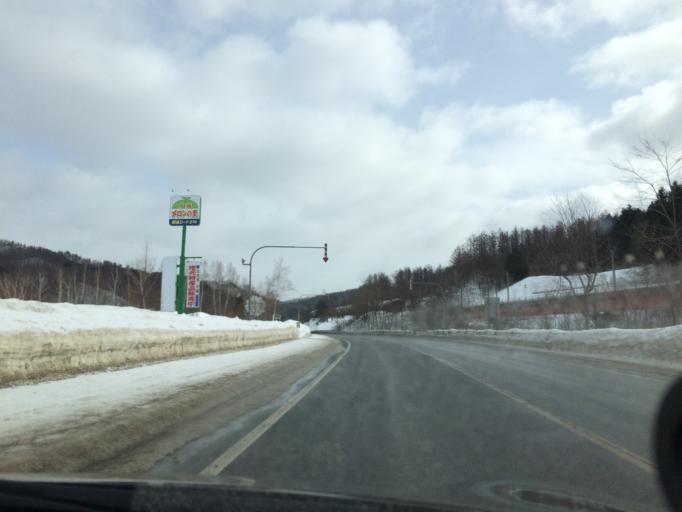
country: JP
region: Hokkaido
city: Iwamizawa
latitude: 42.9331
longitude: 142.0846
